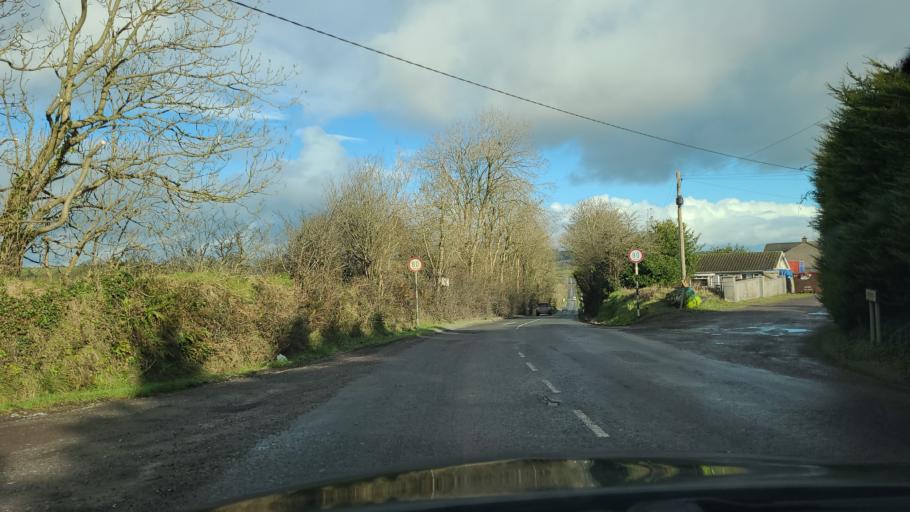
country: IE
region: Munster
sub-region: County Cork
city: Bandon
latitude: 51.7596
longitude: -8.7292
